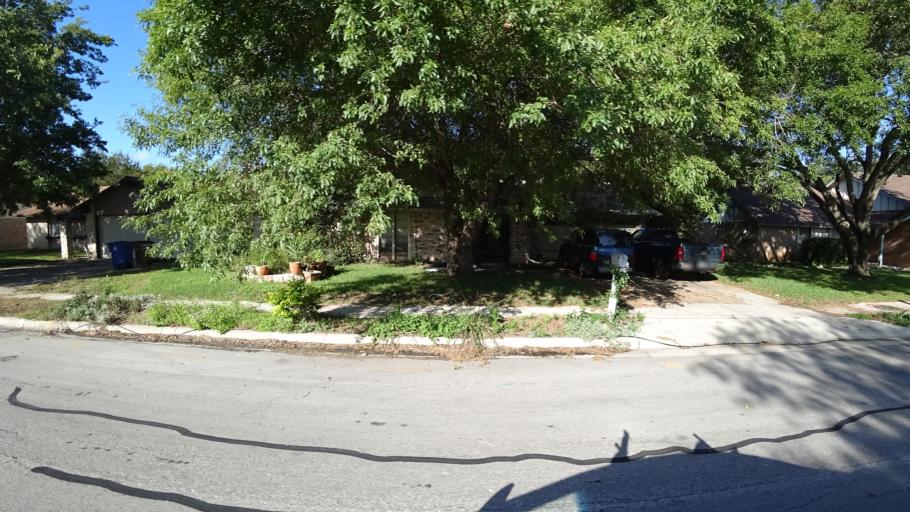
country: US
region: Texas
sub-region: Travis County
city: Rollingwood
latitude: 30.2133
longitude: -97.8133
